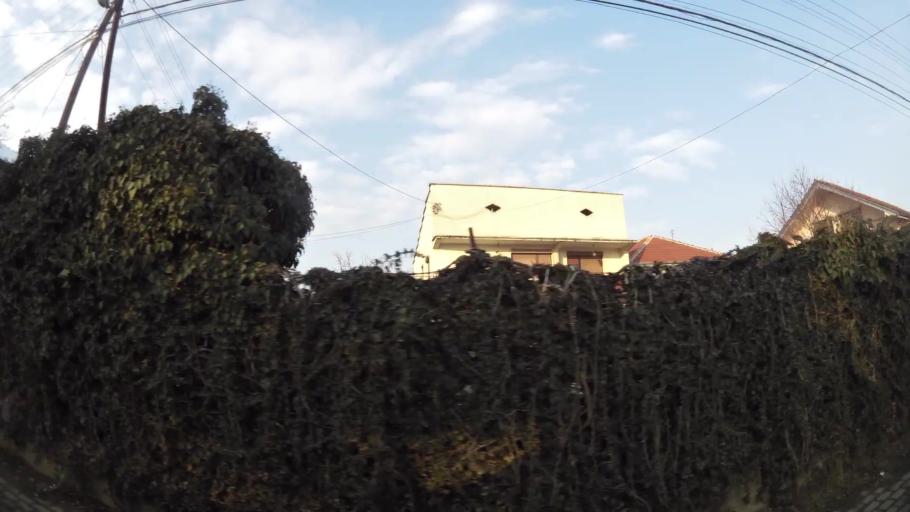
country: MK
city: Creshevo
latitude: 42.0271
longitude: 21.5250
